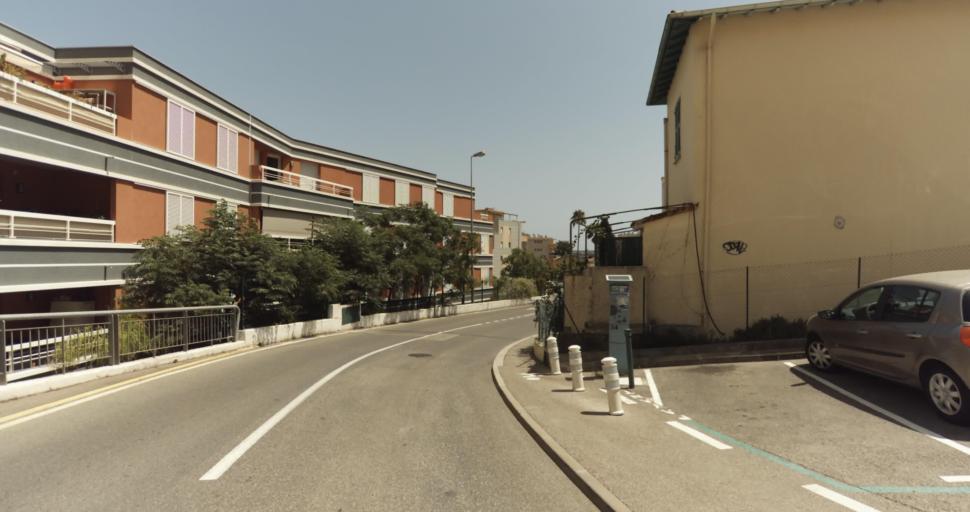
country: FR
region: Provence-Alpes-Cote d'Azur
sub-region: Departement des Alpes-Maritimes
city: Roquebrune-Cap-Martin
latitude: 43.7672
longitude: 7.4801
